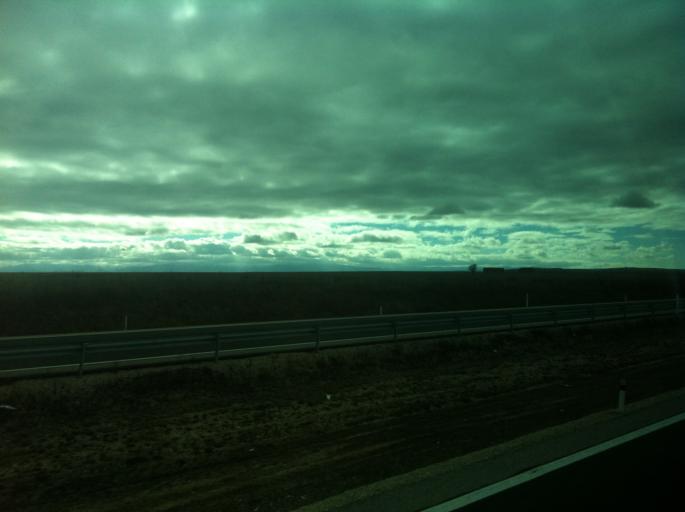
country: ES
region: Castille and Leon
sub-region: Provincia de Burgos
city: Grisalena
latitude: 42.5613
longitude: -3.2705
